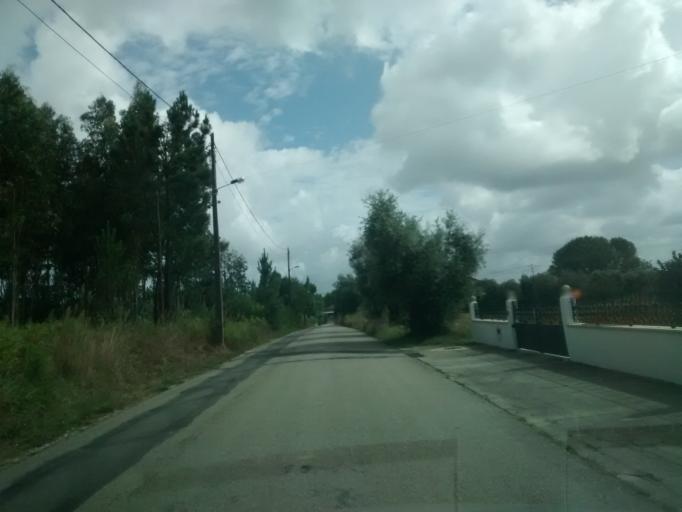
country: PT
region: Aveiro
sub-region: Anadia
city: Sangalhos
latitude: 40.4798
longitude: -8.4944
